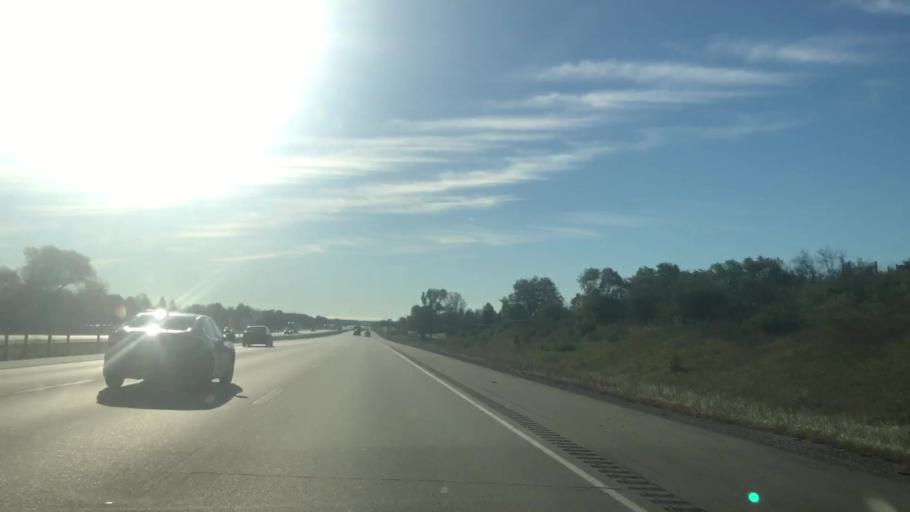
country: US
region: Wisconsin
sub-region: Washington County
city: Richfield
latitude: 43.2359
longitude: -88.1743
